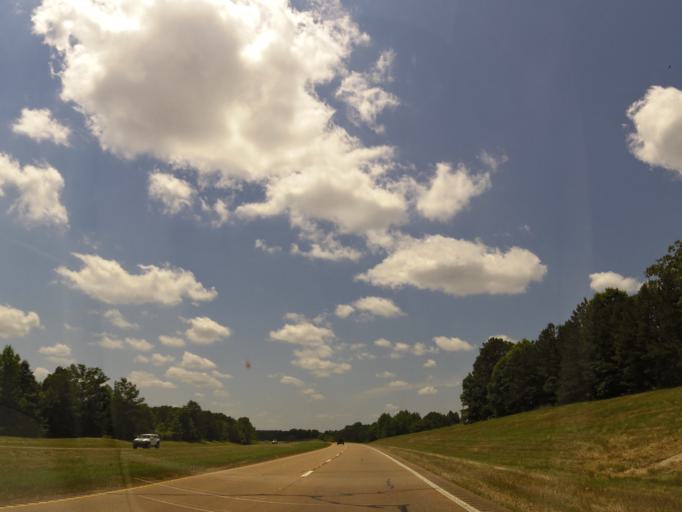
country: US
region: Mississippi
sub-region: Pontotoc County
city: Pontotoc
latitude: 34.2857
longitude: -89.0869
